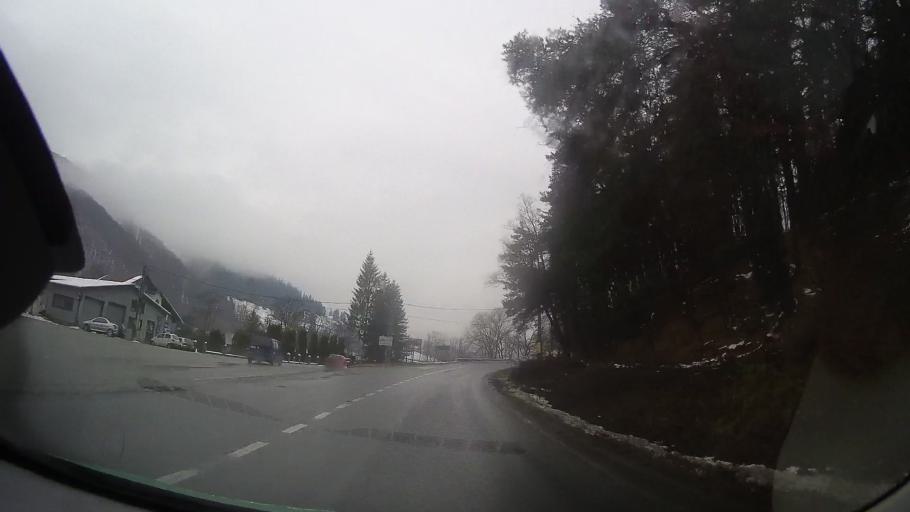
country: RO
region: Neamt
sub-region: Comuna Tarcau
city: Tarcau
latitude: 46.8917
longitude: 26.1250
